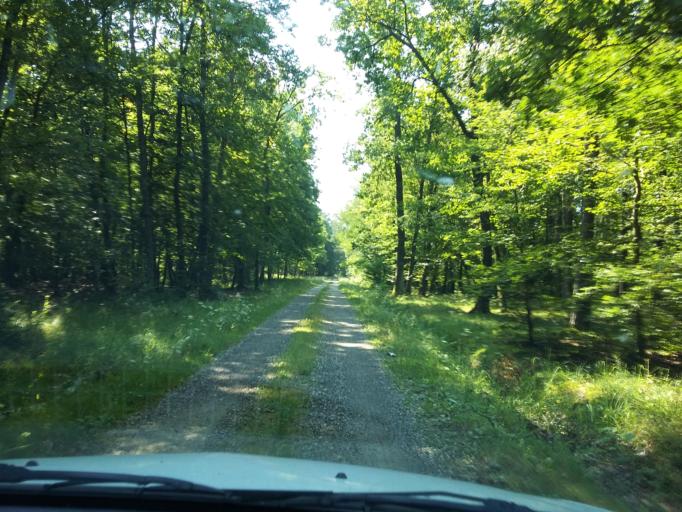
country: SI
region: Salovci
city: Salovci
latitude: 46.8556
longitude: 16.3173
